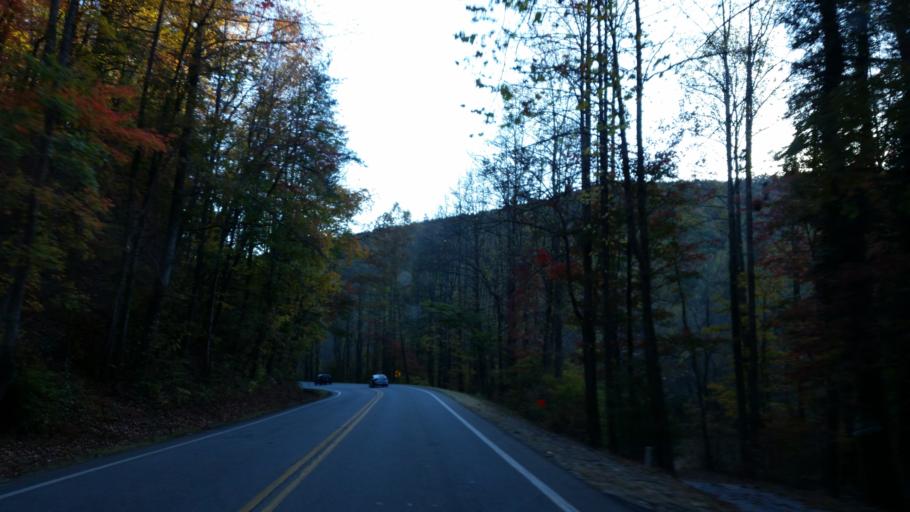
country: US
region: Georgia
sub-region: Pickens County
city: Jasper
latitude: 34.5692
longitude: -84.3086
